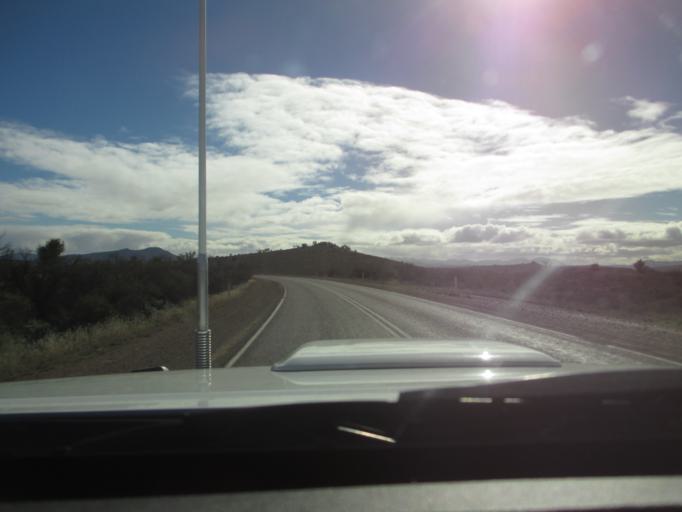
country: AU
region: South Australia
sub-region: Flinders Ranges
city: Quorn
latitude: -31.9043
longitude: 138.4352
